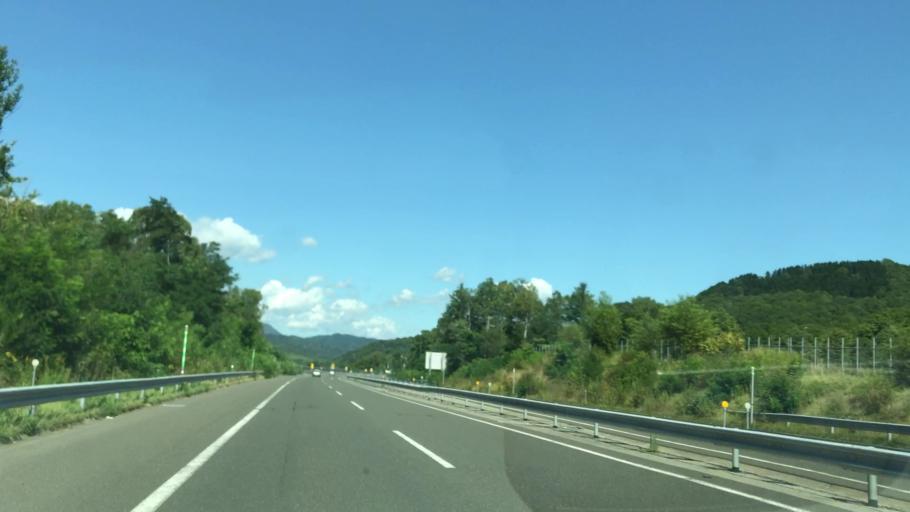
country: JP
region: Hokkaido
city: Shimo-furano
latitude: 42.9894
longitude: 142.4111
